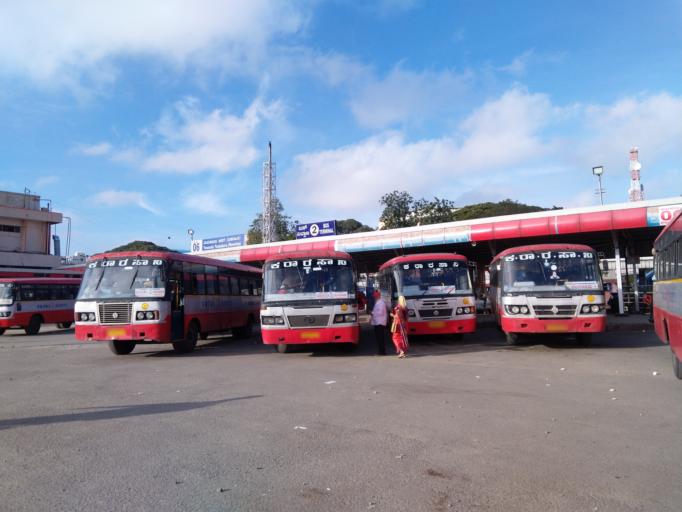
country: IN
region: Karnataka
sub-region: Bangalore Urban
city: Bangalore
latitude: 12.9771
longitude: 77.5718
